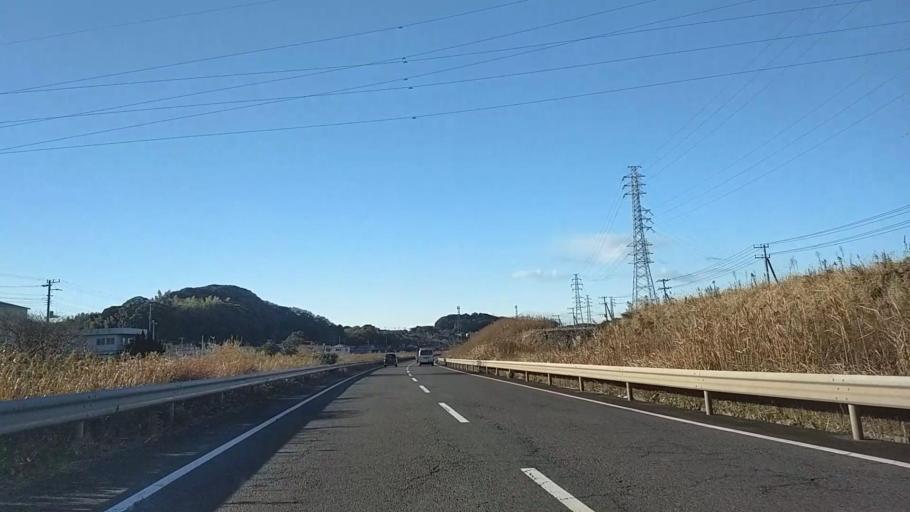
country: JP
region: Chiba
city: Kisarazu
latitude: 35.3580
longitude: 139.9095
